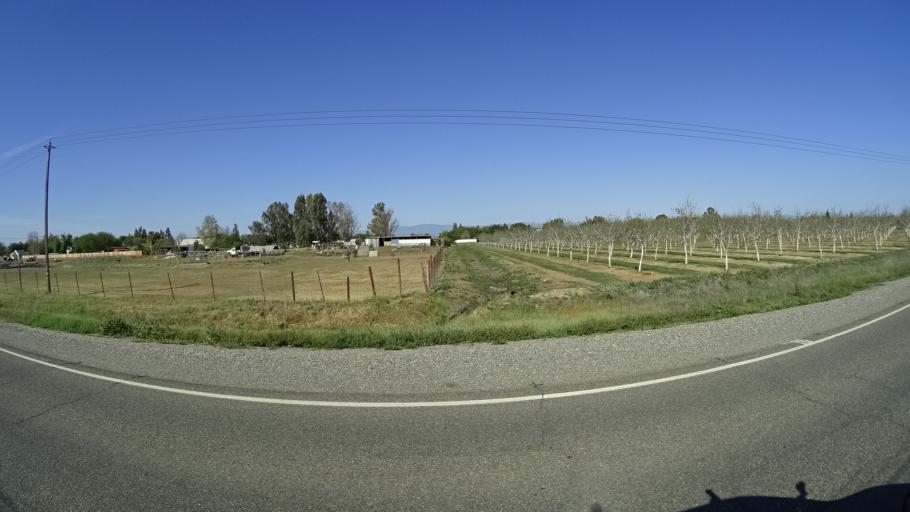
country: US
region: California
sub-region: Glenn County
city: Willows
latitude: 39.5407
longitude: -122.1934
